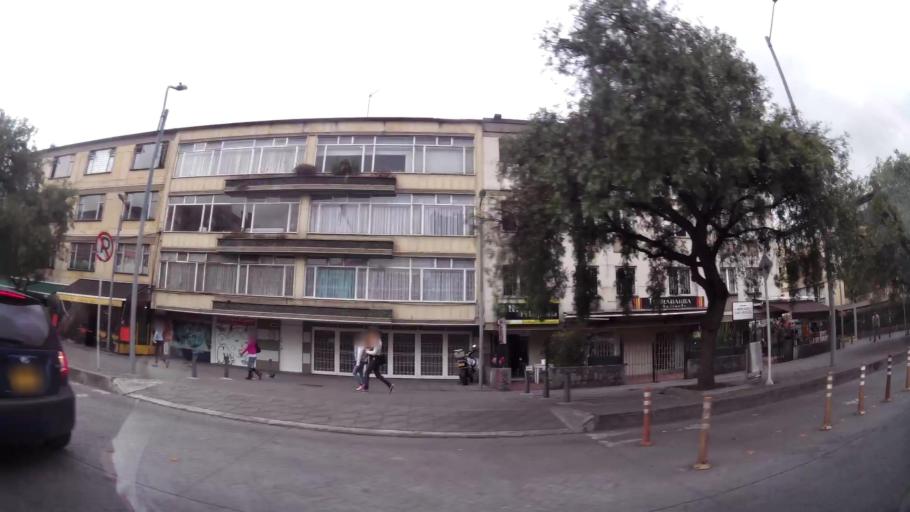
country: CO
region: Bogota D.C.
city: Barrio San Luis
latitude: 4.6712
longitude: -74.0579
